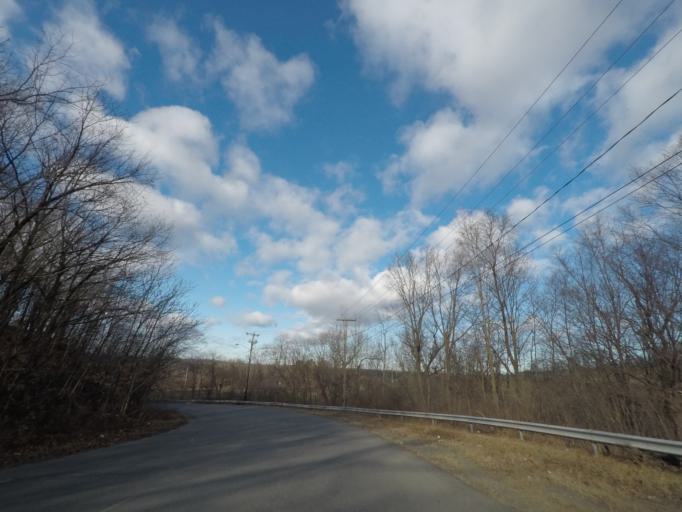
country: US
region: New York
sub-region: Saratoga County
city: Waterford
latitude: 42.7869
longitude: -73.6579
